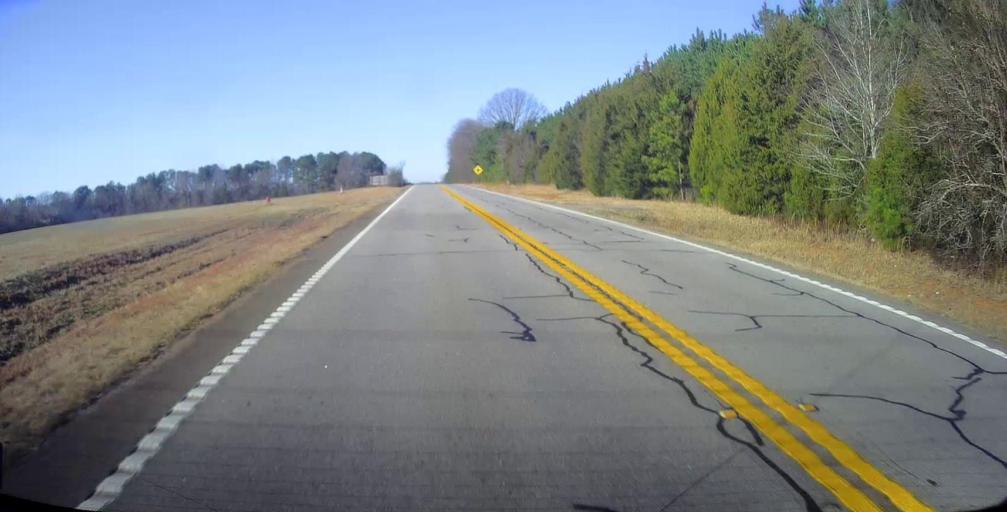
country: US
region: Georgia
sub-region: Meriwether County
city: Manchester
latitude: 32.8985
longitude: -84.5992
